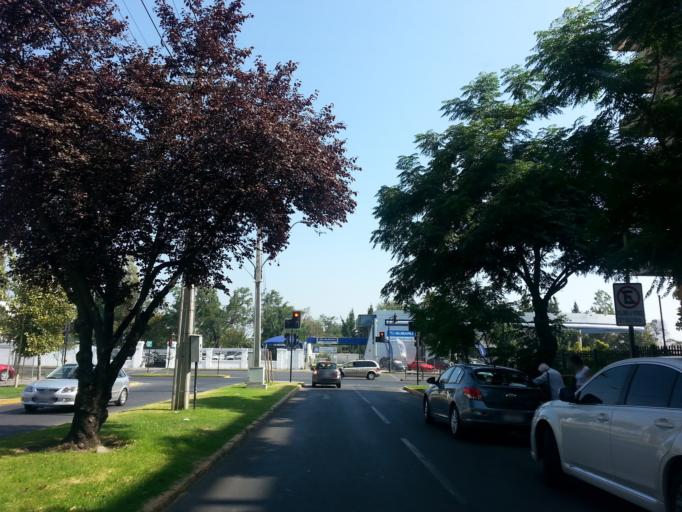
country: CL
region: Santiago Metropolitan
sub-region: Provincia de Santiago
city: Villa Presidente Frei, Nunoa, Santiago, Chile
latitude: -33.4306
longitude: -70.5703
